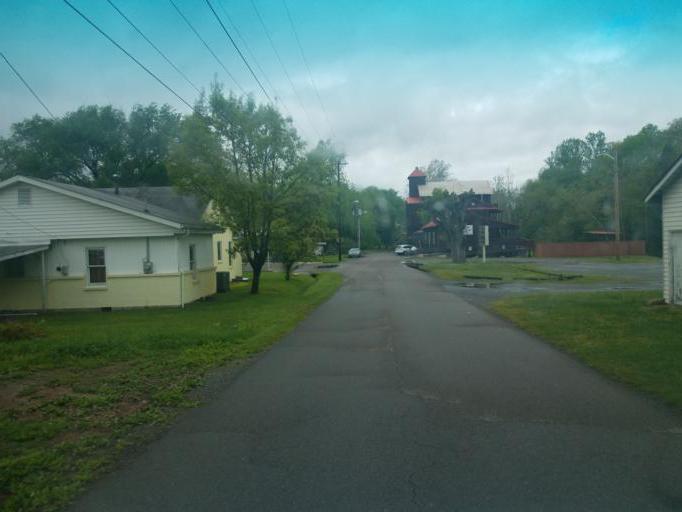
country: US
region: Virginia
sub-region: Washington County
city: Emory
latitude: 36.6361
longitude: -81.7890
